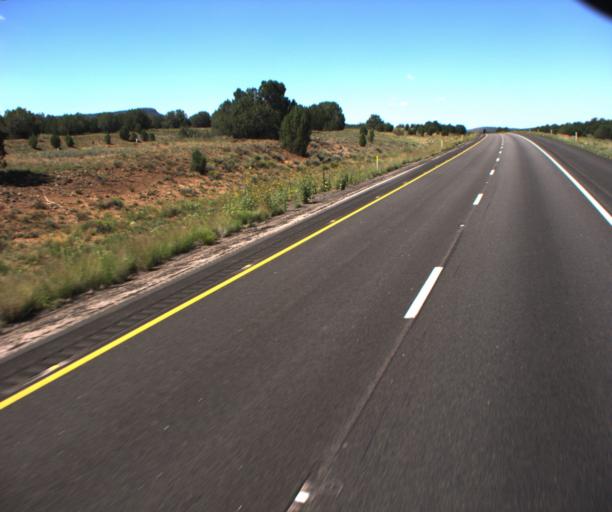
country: US
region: Arizona
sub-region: Mohave County
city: Peach Springs
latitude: 35.2254
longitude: -113.2378
